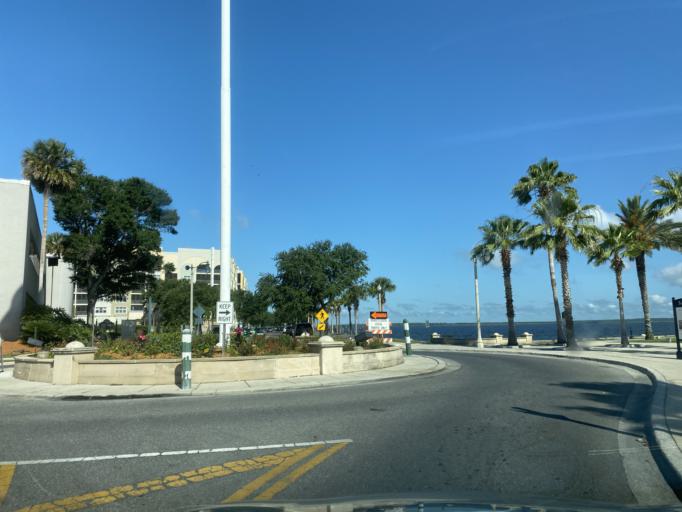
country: US
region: Florida
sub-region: Seminole County
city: Sanford
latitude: 28.8146
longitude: -81.2678
